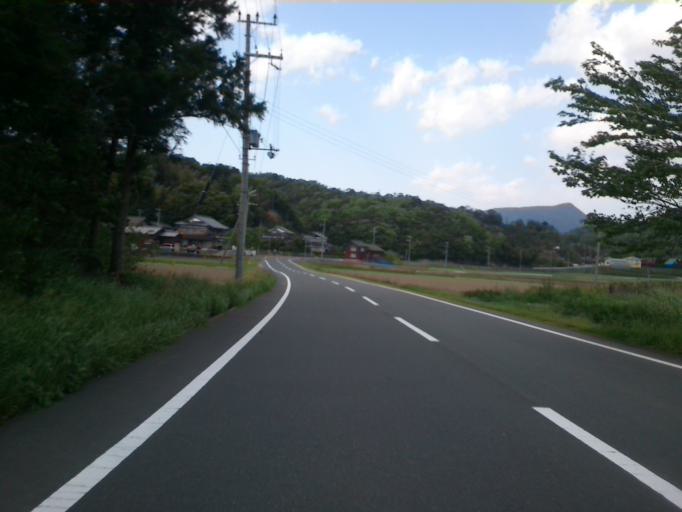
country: JP
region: Kyoto
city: Miyazu
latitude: 35.6933
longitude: 135.0979
